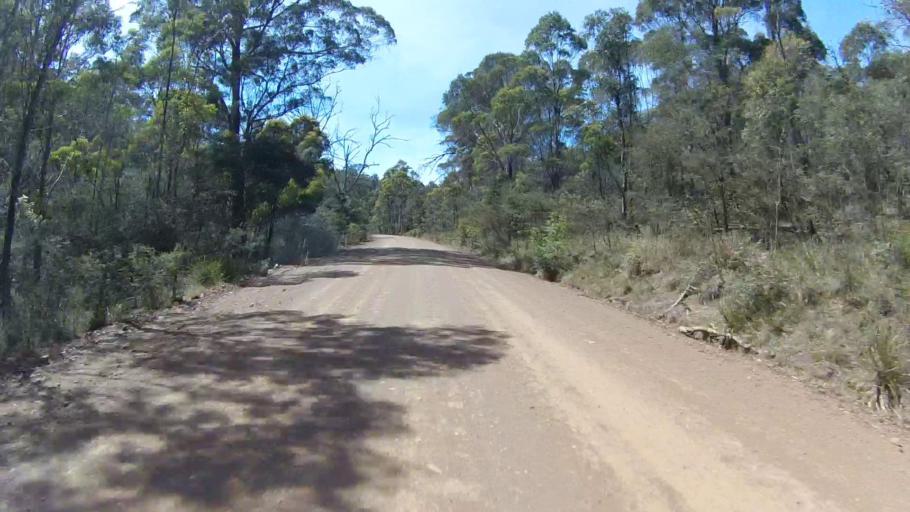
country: AU
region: Tasmania
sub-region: Sorell
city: Sorell
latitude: -42.6427
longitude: 147.7381
